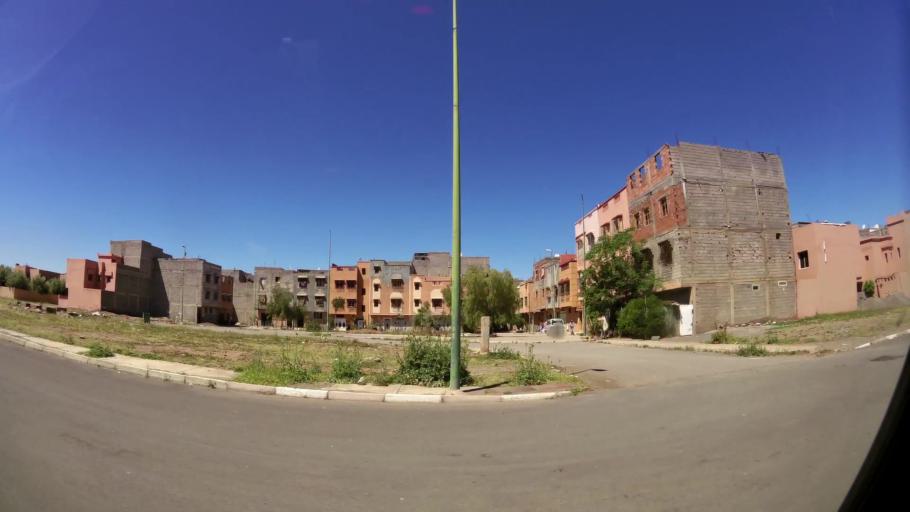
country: MA
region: Marrakech-Tensift-Al Haouz
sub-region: Marrakech
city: Marrakesh
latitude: 31.5720
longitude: -7.9847
